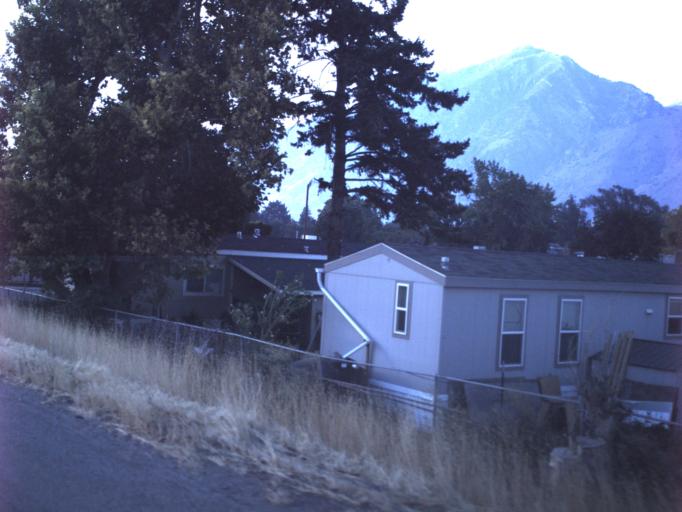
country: US
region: Utah
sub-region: Utah County
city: Springville
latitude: 40.1521
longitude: -111.6063
